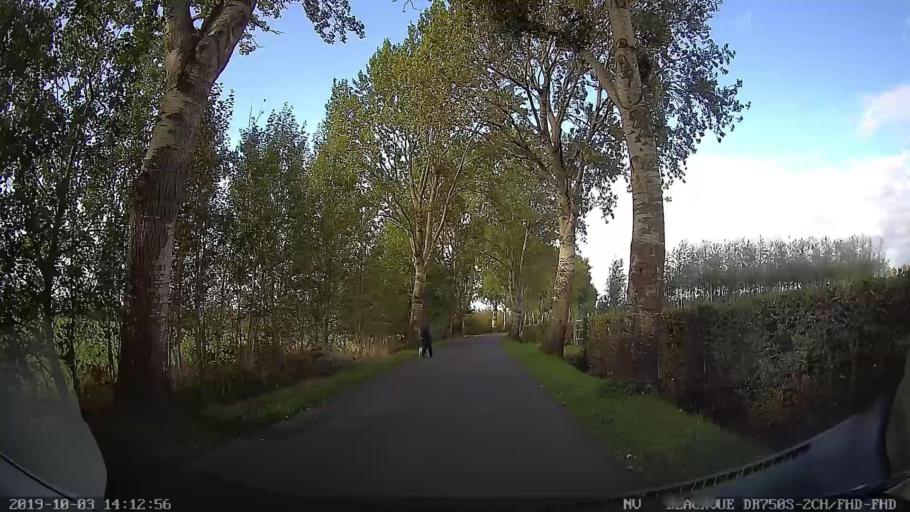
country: DE
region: Schleswig-Holstein
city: Tangstedt
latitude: 53.6640
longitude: 9.8313
